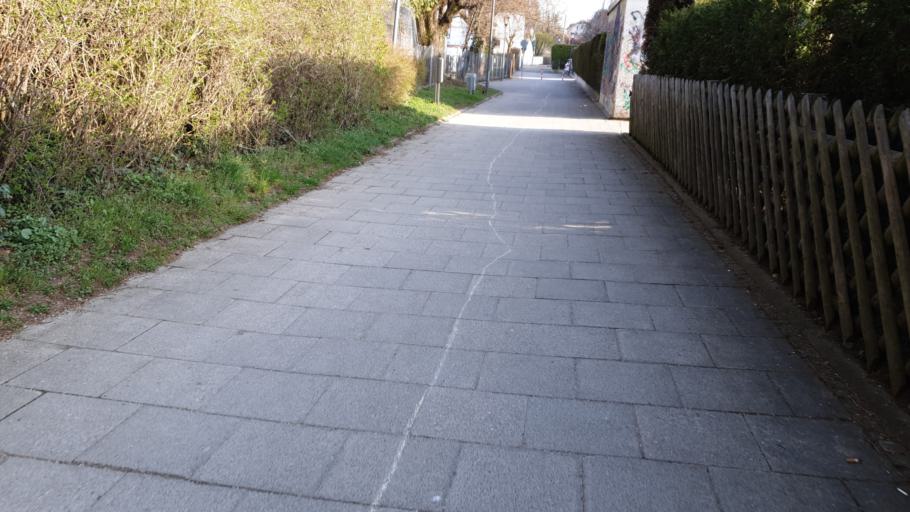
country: DE
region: Bavaria
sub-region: Upper Bavaria
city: Germering
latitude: 48.1621
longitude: 11.4114
